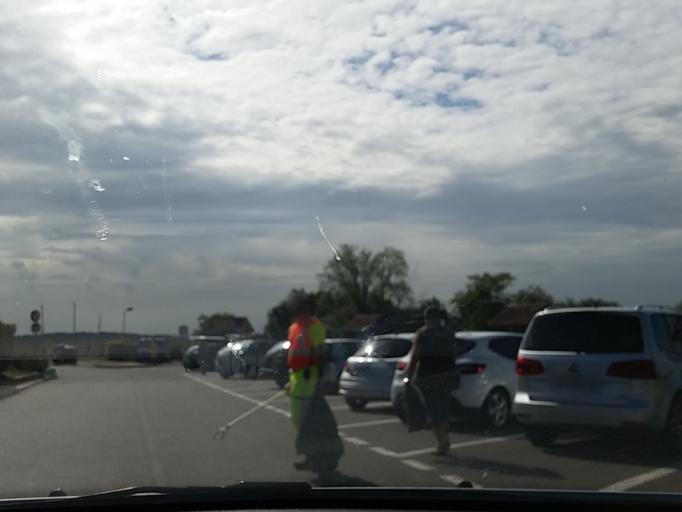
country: FR
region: Centre
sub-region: Departement du Cher
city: Orval
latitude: 46.7521
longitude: 2.4149
